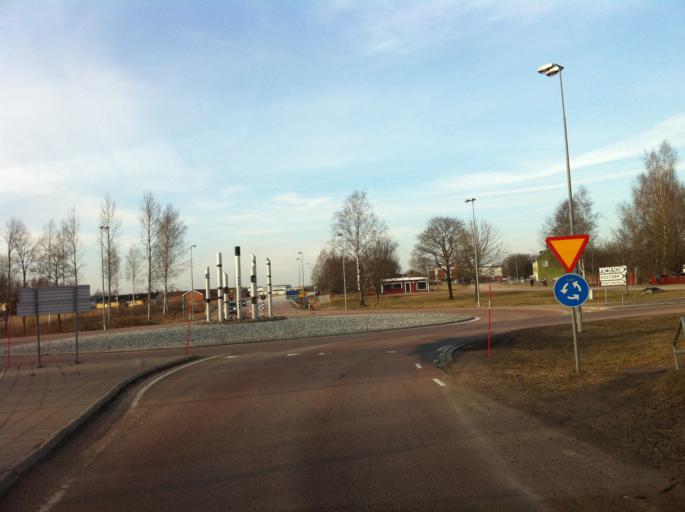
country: SE
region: Vaermland
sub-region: Storfors Kommun
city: Storfors
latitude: 59.5390
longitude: 14.2797
